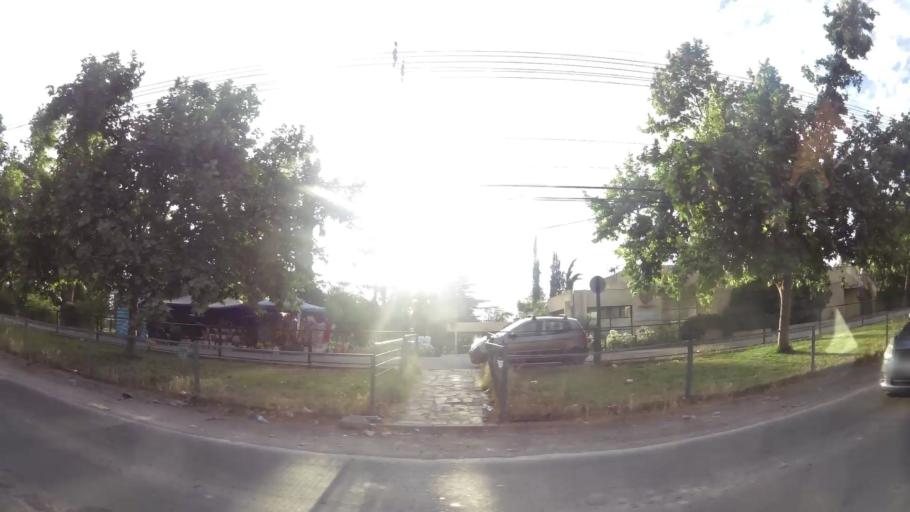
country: CL
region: Santiago Metropolitan
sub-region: Provincia de Maipo
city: San Bernardo
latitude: -33.6223
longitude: -70.6810
